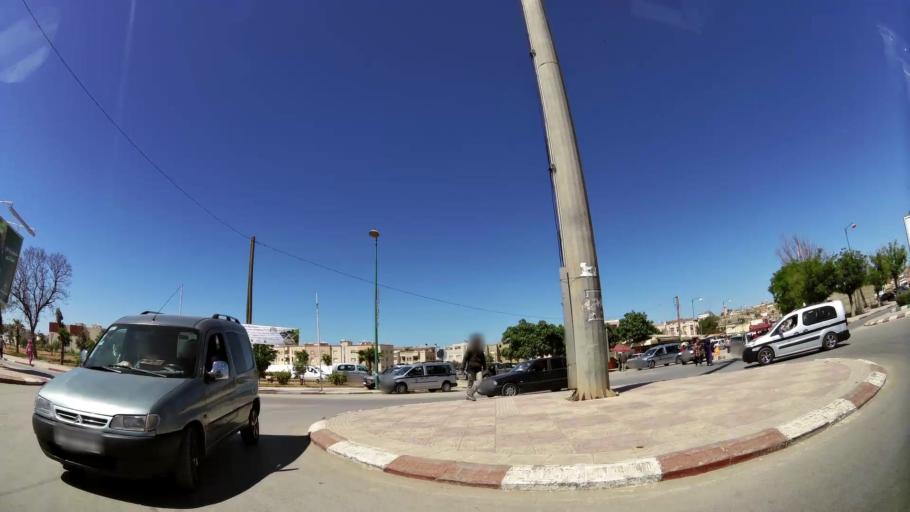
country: MA
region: Meknes-Tafilalet
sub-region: Meknes
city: Meknes
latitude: 33.8916
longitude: -5.5742
